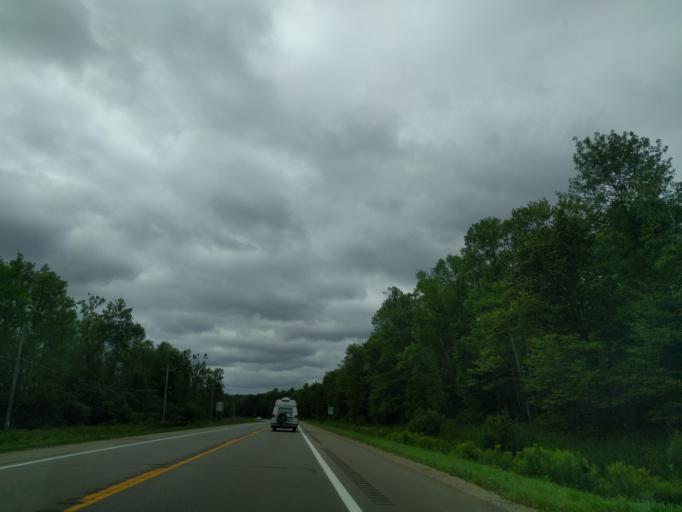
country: US
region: Michigan
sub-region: Menominee County
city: Menominee
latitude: 45.2089
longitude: -87.5316
